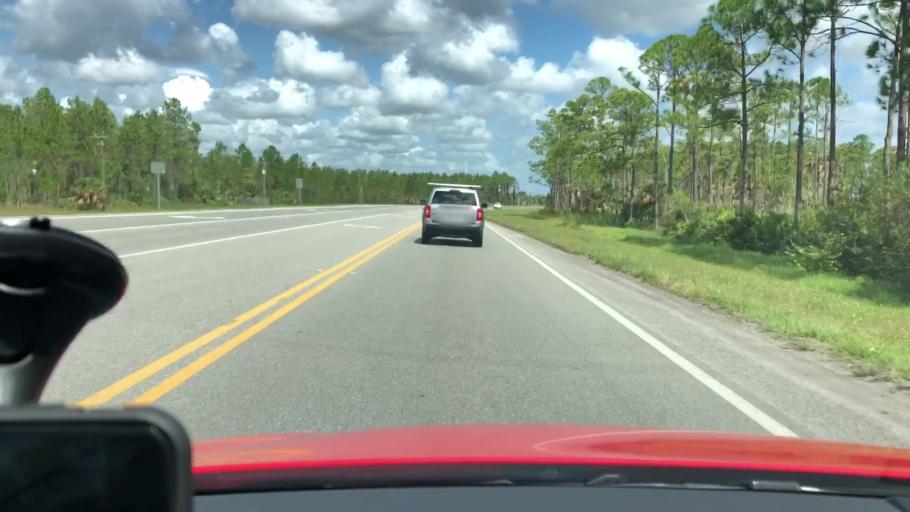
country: US
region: Florida
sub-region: Volusia County
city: Holly Hill
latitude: 29.2086
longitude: -81.1198
